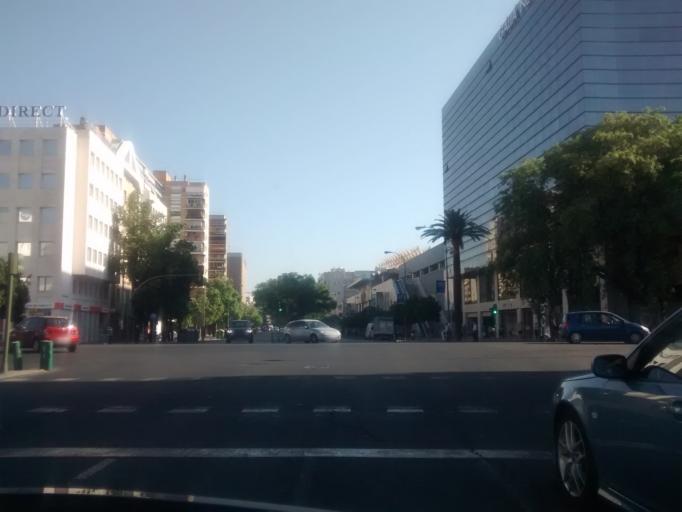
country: ES
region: Andalusia
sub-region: Provincia de Sevilla
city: Sevilla
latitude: 37.3826
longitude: -5.9732
